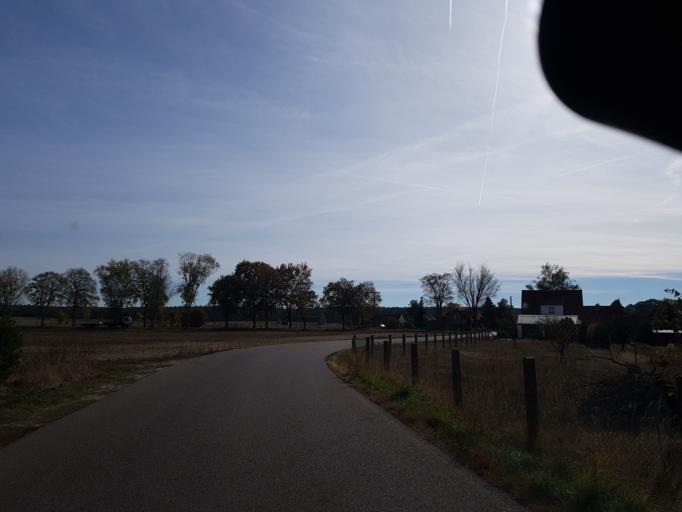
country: DE
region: Brandenburg
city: Schlieben
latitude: 51.7603
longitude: 13.3514
